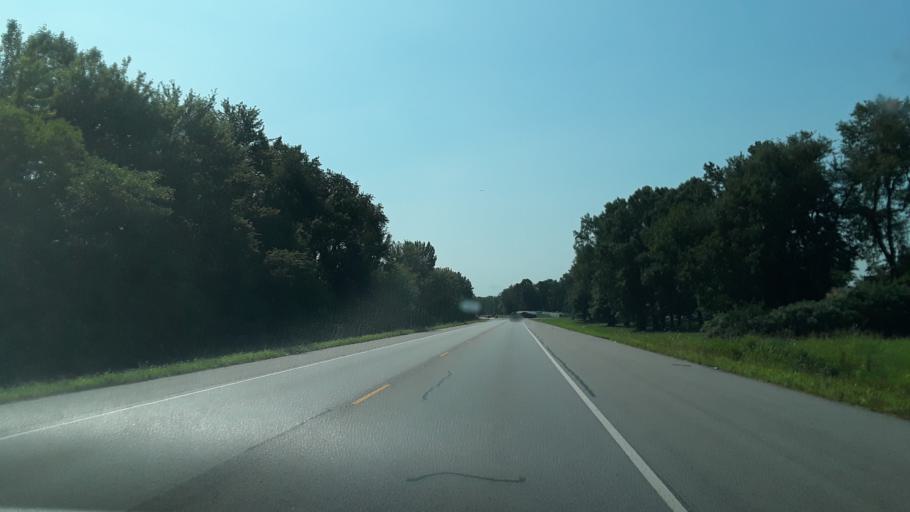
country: US
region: Indiana
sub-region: Clark County
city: Sellersburg
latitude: 38.3772
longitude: -85.7653
